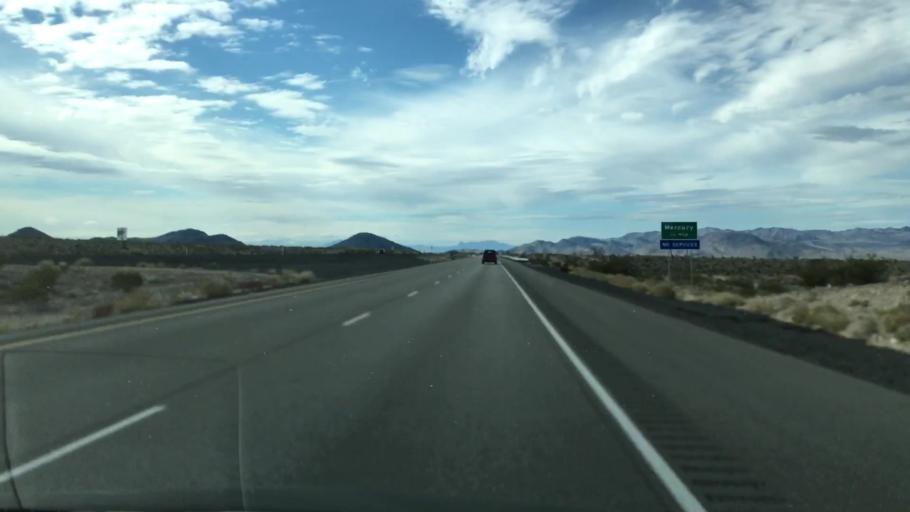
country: US
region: Nevada
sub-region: Nye County
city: Pahrump
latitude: 36.6015
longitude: -115.9869
